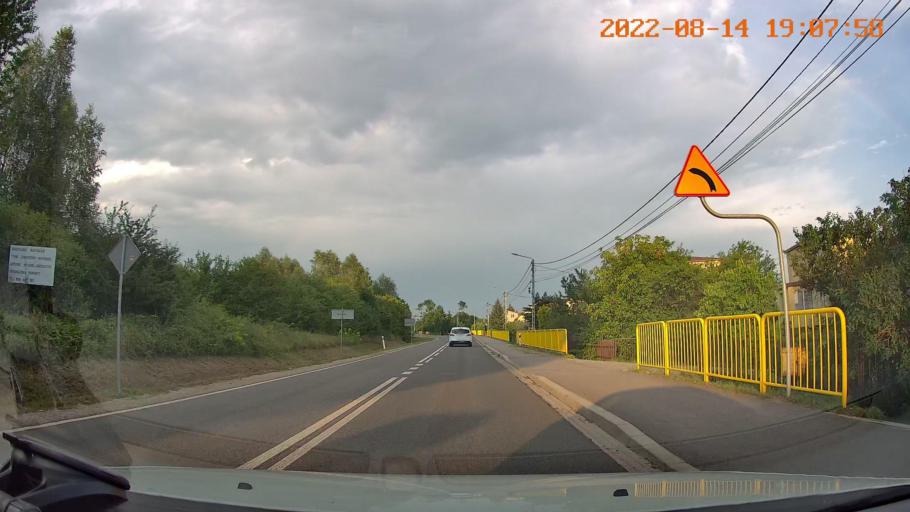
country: PL
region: Swietokrzyskie
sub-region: Powiat kielecki
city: Zagnansk
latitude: 50.9650
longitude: 20.6992
